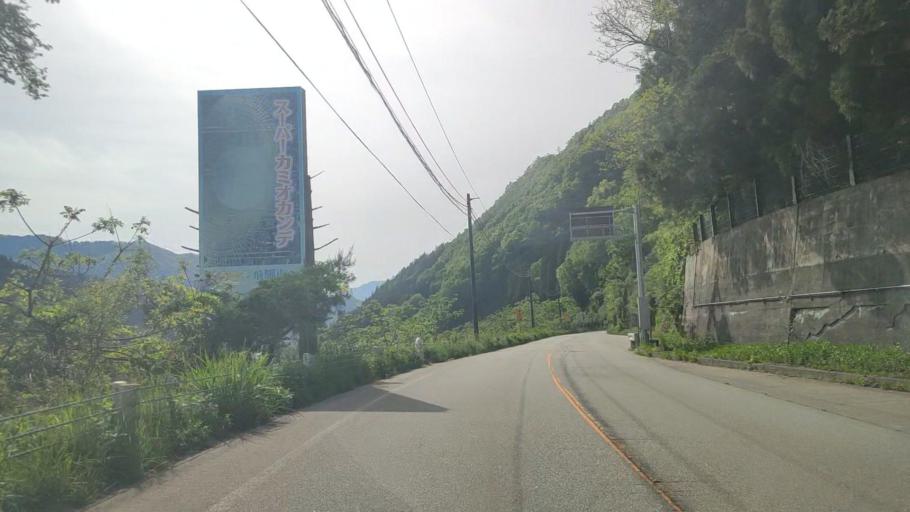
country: JP
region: Gifu
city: Takayama
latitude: 36.2963
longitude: 137.3665
